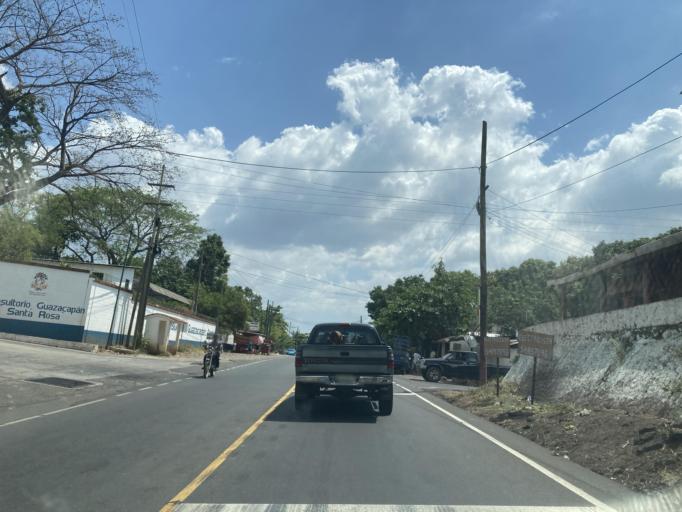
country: GT
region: Santa Rosa
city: Guazacapan
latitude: 14.0684
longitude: -90.4149
